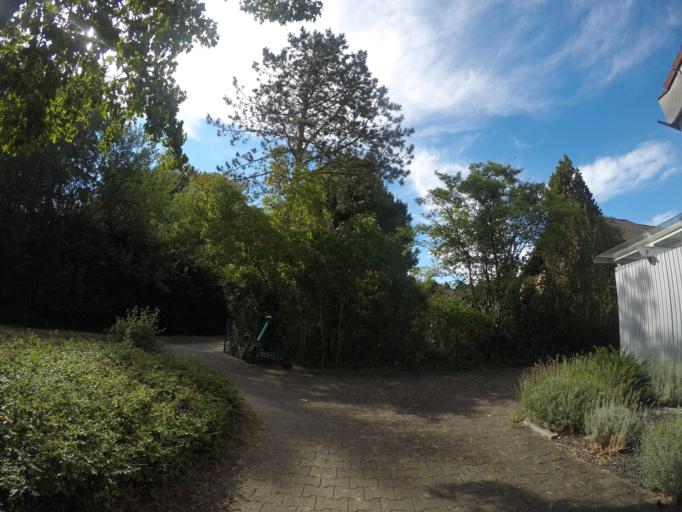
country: DE
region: Baden-Wuerttemberg
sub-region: Tuebingen Region
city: Staig
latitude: 48.3444
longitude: 9.9725
